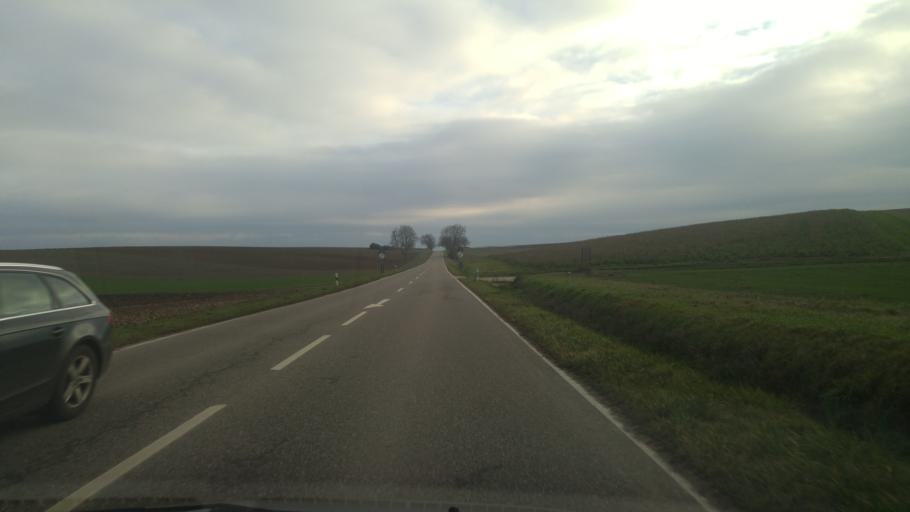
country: DE
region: Rheinland-Pfalz
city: Winden
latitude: 49.0849
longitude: 8.1269
